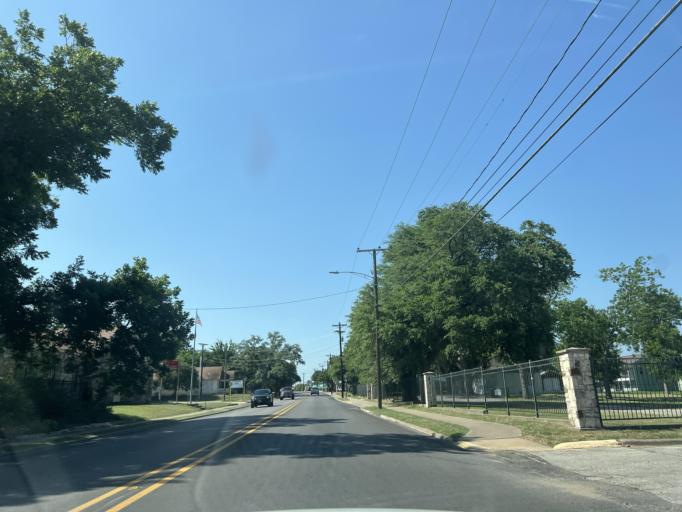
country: US
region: Texas
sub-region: Washington County
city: Brenham
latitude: 30.1737
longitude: -96.3998
